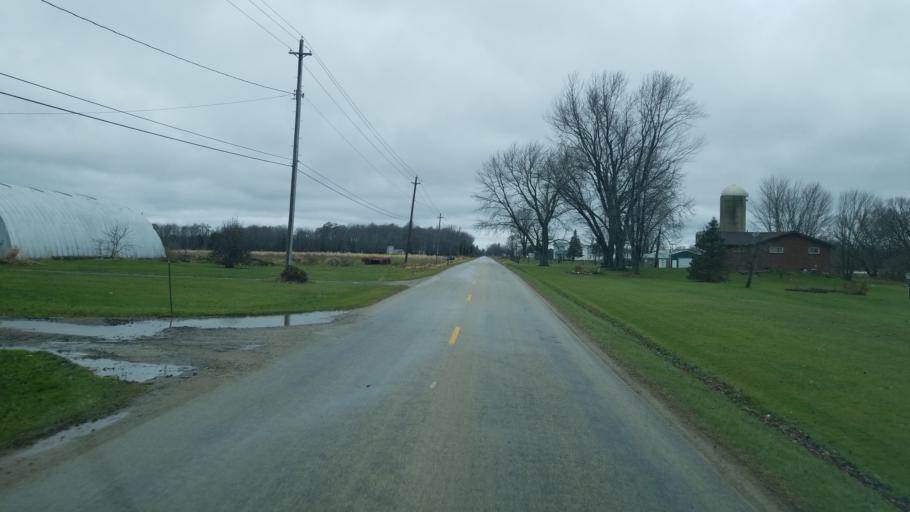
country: US
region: Ohio
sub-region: Ashtabula County
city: Jefferson
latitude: 41.7710
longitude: -80.6231
